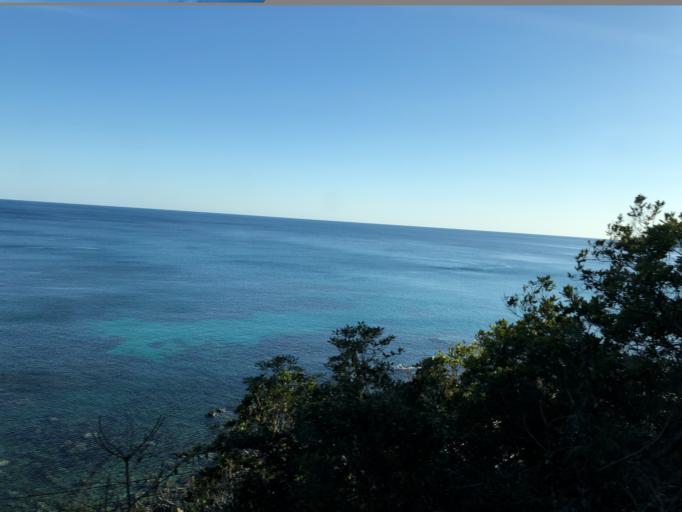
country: JP
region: Kochi
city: Nakamura
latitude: 33.0615
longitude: 133.1029
